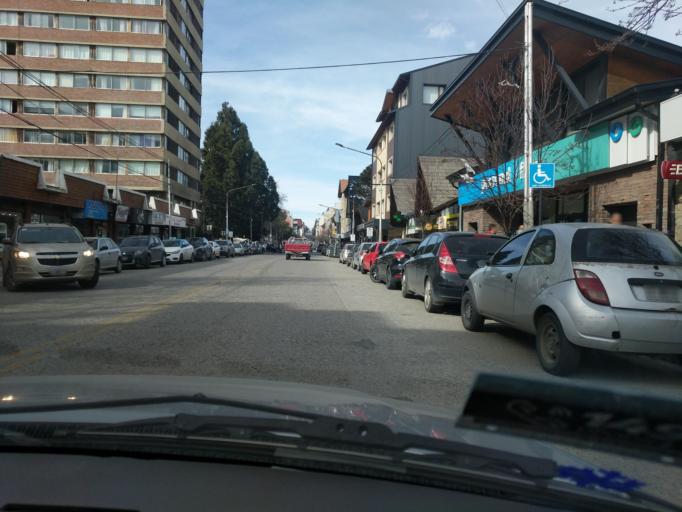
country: AR
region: Rio Negro
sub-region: Departamento de Bariloche
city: San Carlos de Bariloche
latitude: -41.1343
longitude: -71.3125
